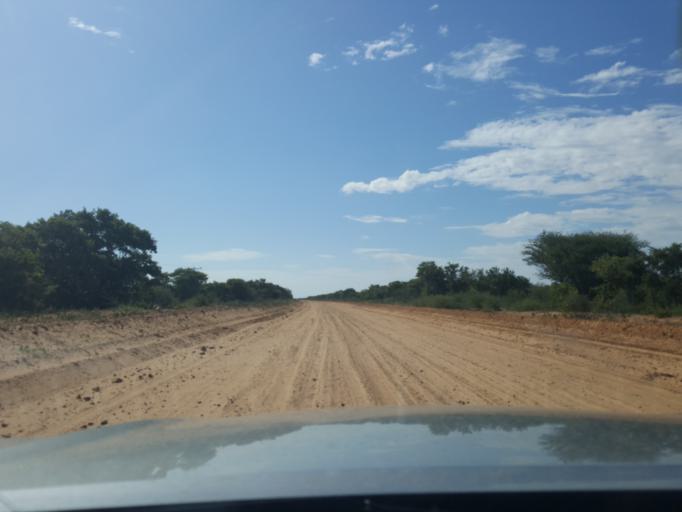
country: BW
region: Kweneng
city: Khudumelapye
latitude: -23.7249
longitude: 24.7403
